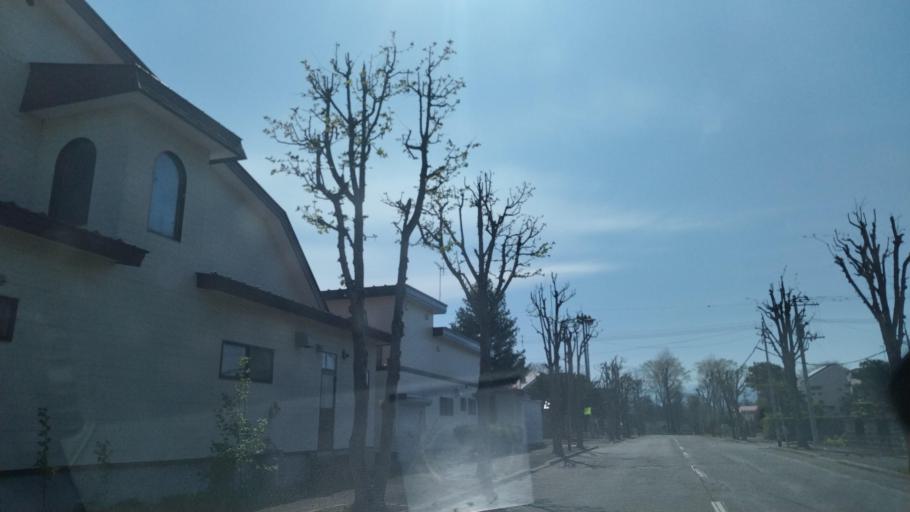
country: JP
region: Hokkaido
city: Obihiro
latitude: 42.9199
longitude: 143.0553
